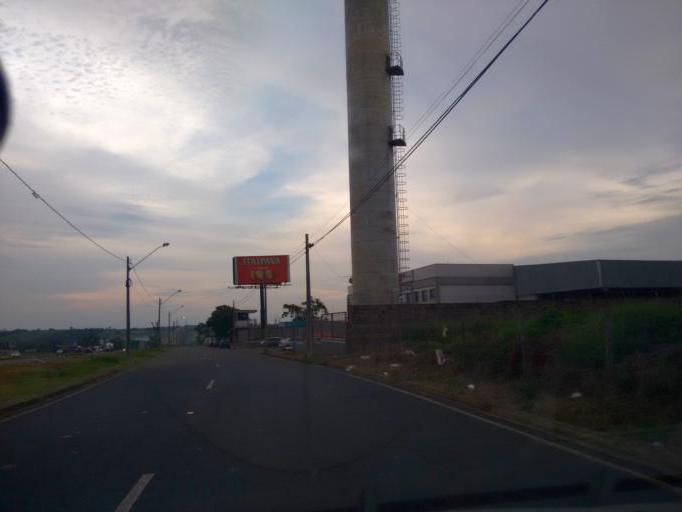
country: BR
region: Sao Paulo
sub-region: Araraquara
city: Araraquara
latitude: -21.7815
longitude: -48.2266
